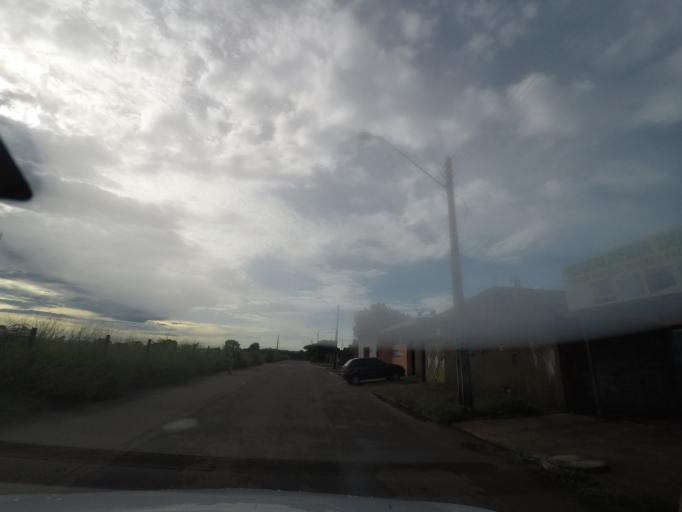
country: BR
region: Goias
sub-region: Aparecida De Goiania
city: Aparecida de Goiania
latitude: -16.7769
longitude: -49.3863
